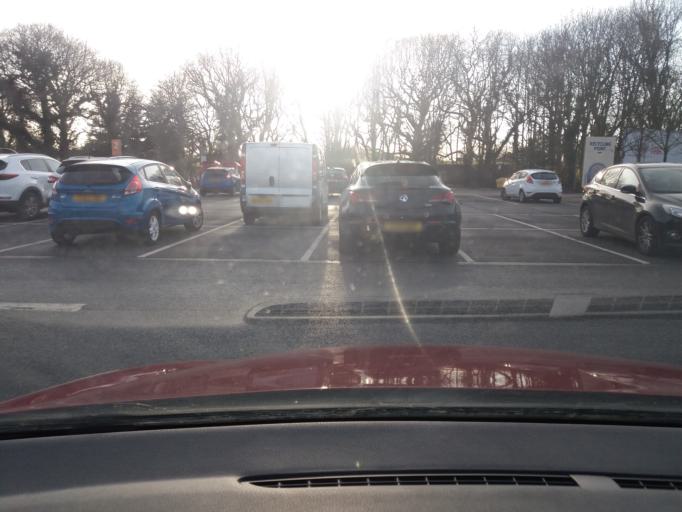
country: GB
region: England
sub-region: Lancashire
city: Euxton
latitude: 53.6570
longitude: -2.6590
